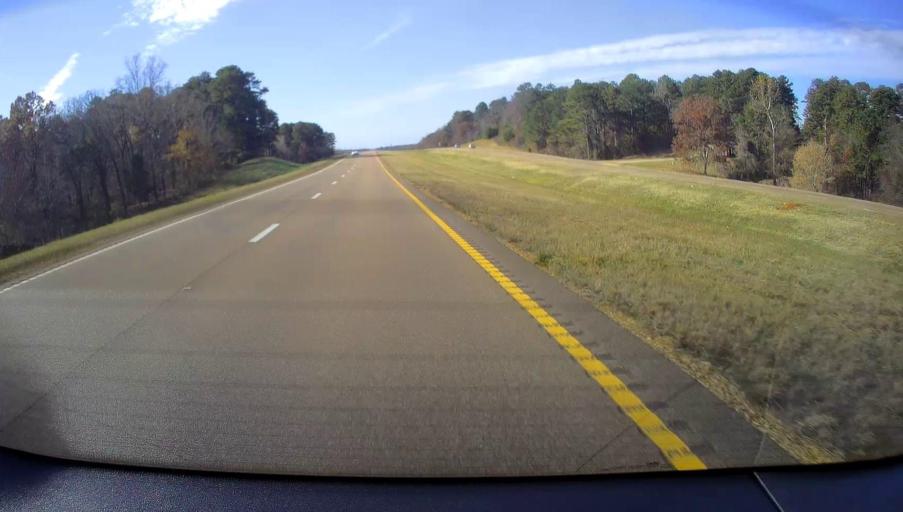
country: US
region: Mississippi
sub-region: Benton County
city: Ashland
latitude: 34.9538
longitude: -89.0366
